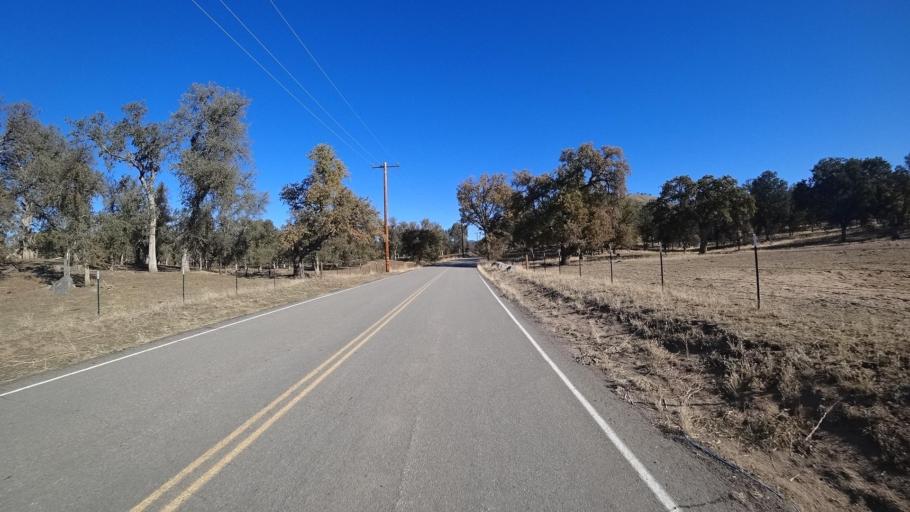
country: US
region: California
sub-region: Kern County
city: Alta Sierra
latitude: 35.7748
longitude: -118.7073
